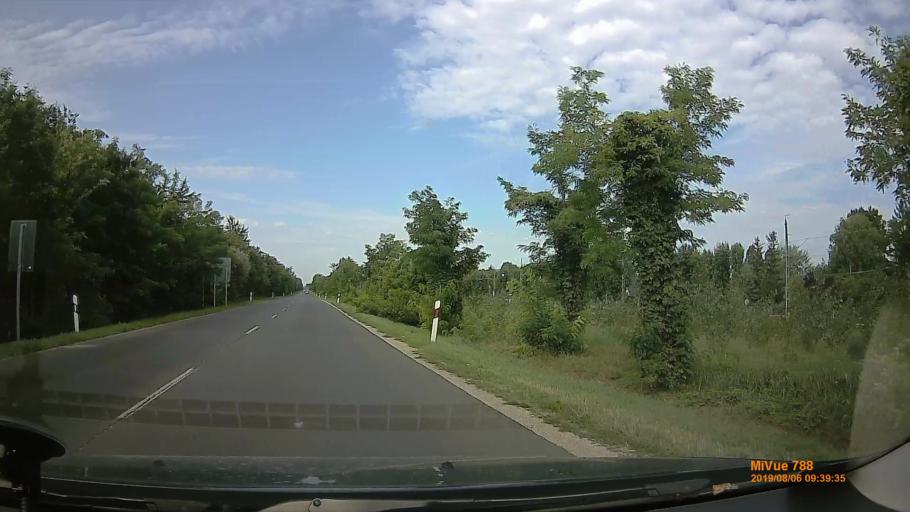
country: HU
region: Somogy
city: Balatonlelle
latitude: 46.8013
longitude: 17.7447
